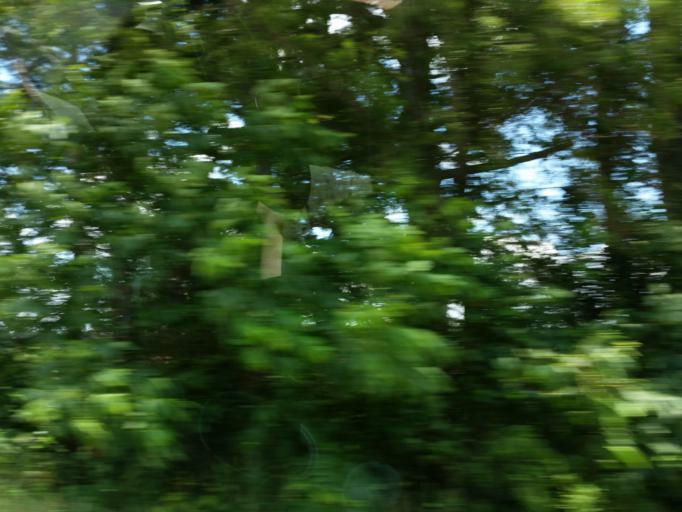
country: US
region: Kentucky
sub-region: Fulton County
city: Hickman
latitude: 36.5498
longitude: -89.2395
